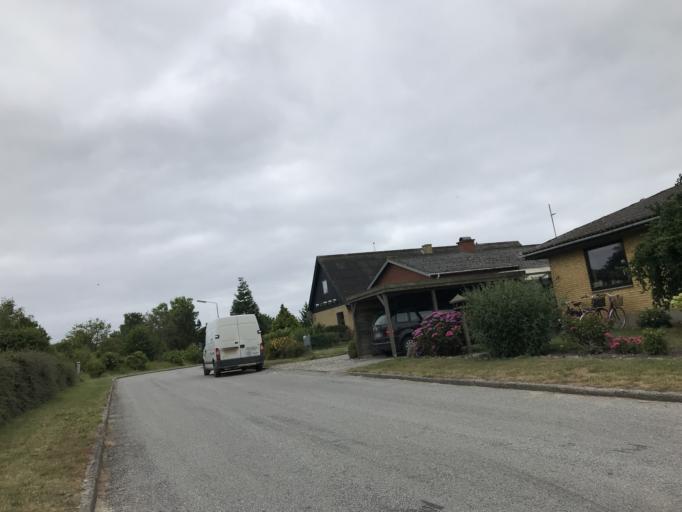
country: DK
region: South Denmark
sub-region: Faaborg-Midtfyn Kommune
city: Faaborg
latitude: 54.9408
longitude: 10.2531
